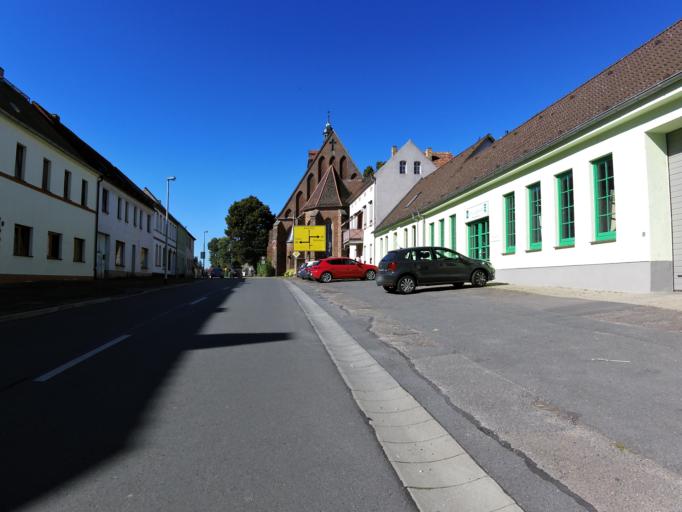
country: DE
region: Saxony
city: Dommitzsch
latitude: 51.6403
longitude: 12.8849
